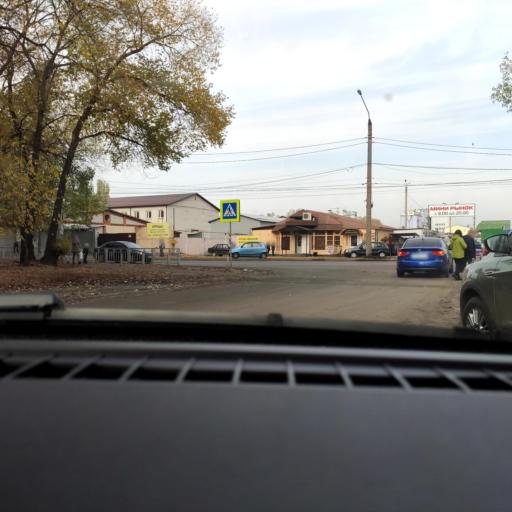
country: RU
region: Voronezj
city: Maslovka
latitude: 51.6340
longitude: 39.2772
